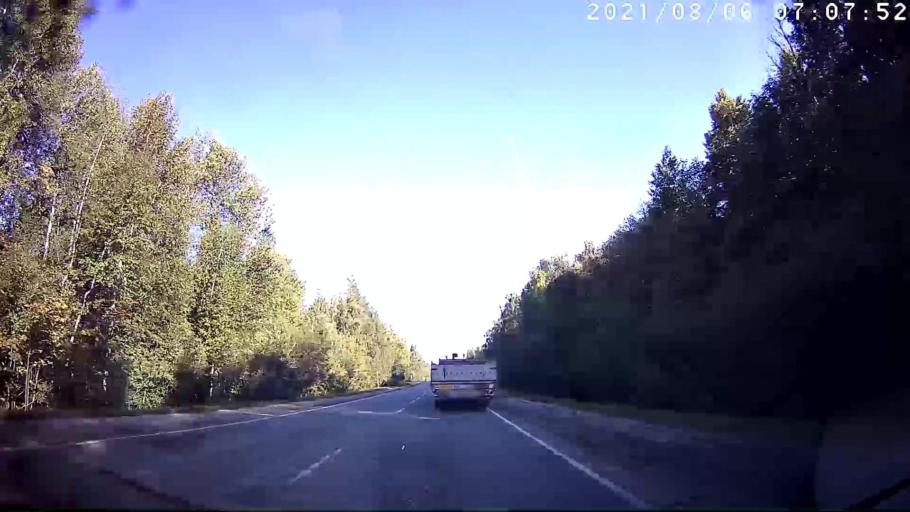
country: RU
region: Mariy-El
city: Yoshkar-Ola
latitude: 56.5659
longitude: 47.9760
